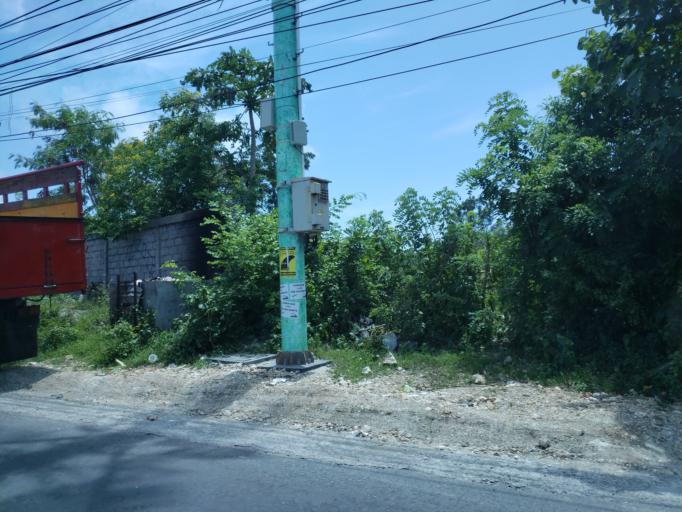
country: ID
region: Bali
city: Kangin
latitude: -8.8299
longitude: 115.1352
